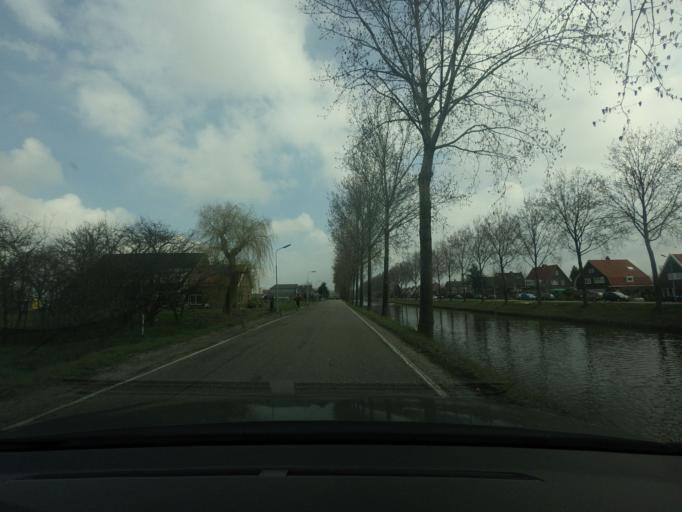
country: NL
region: North Holland
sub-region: Gemeente Haarlemmermeer
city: Hoofddorp
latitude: 52.3495
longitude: 4.7553
